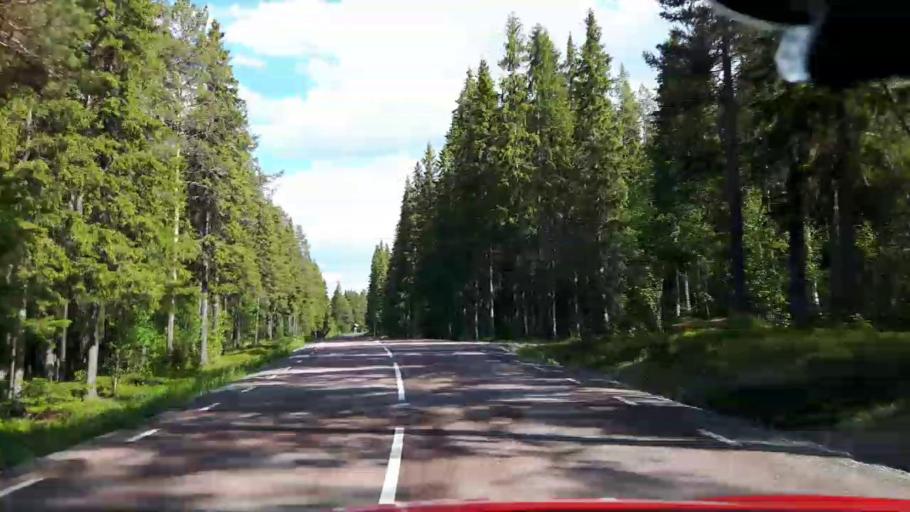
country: SE
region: Jaemtland
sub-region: Krokoms Kommun
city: Valla
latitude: 63.9604
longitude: 14.1839
